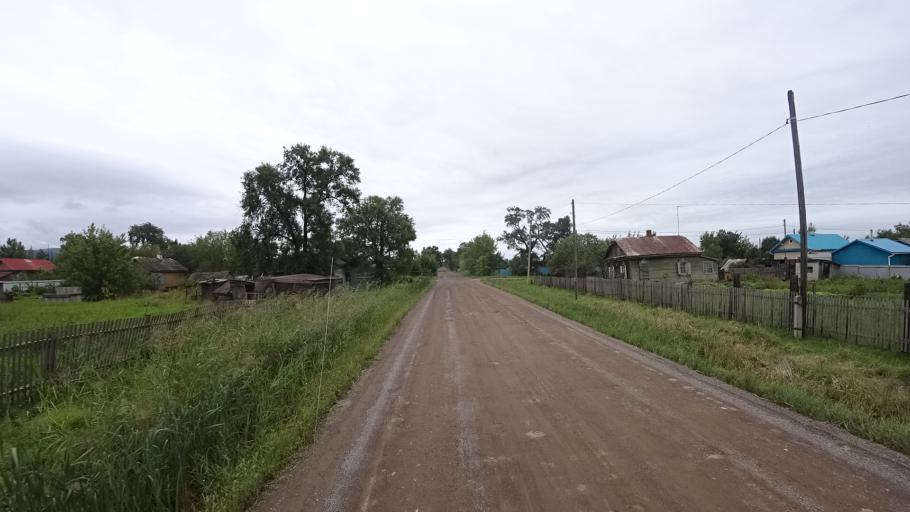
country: RU
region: Primorskiy
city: Chernigovka
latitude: 44.3402
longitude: 132.5680
